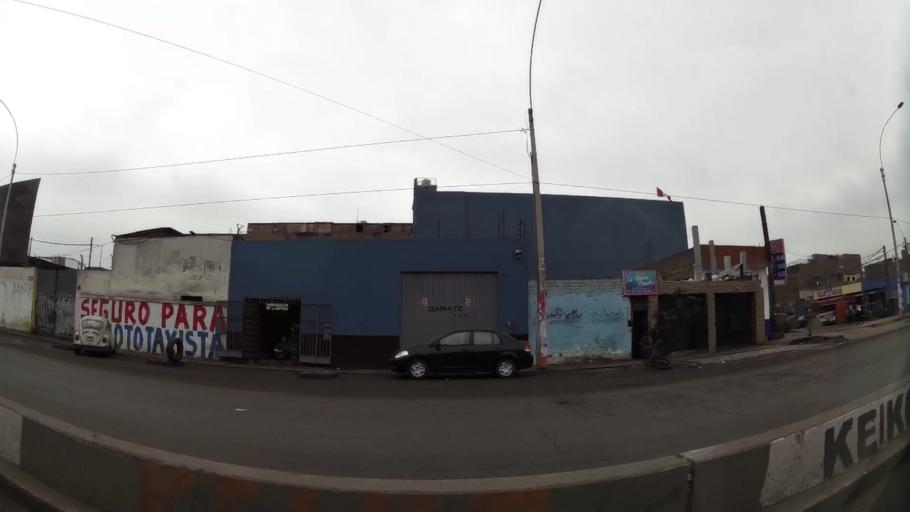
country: PE
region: Lima
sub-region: Lima
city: San Luis
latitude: -12.0655
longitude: -77.0049
